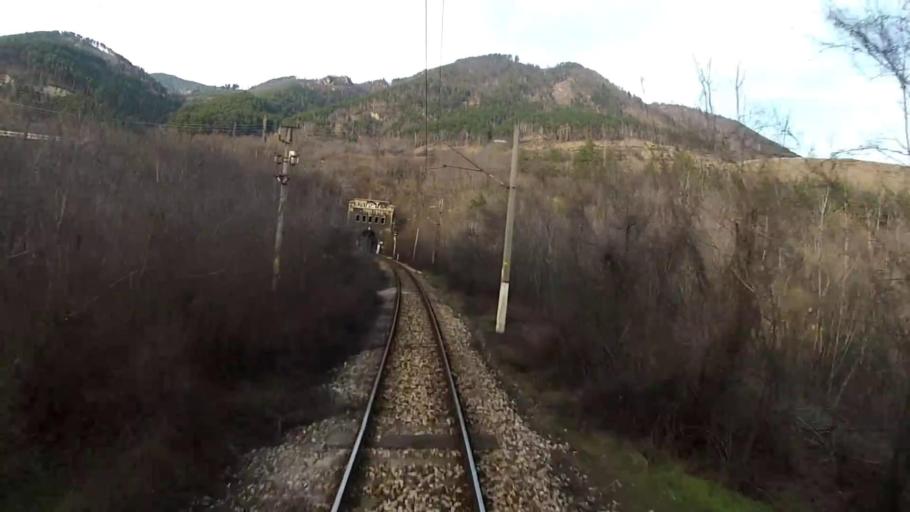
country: BG
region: Plovdiv
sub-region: Obshtina Karlovo
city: Klisura
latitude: 42.6899
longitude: 24.4559
